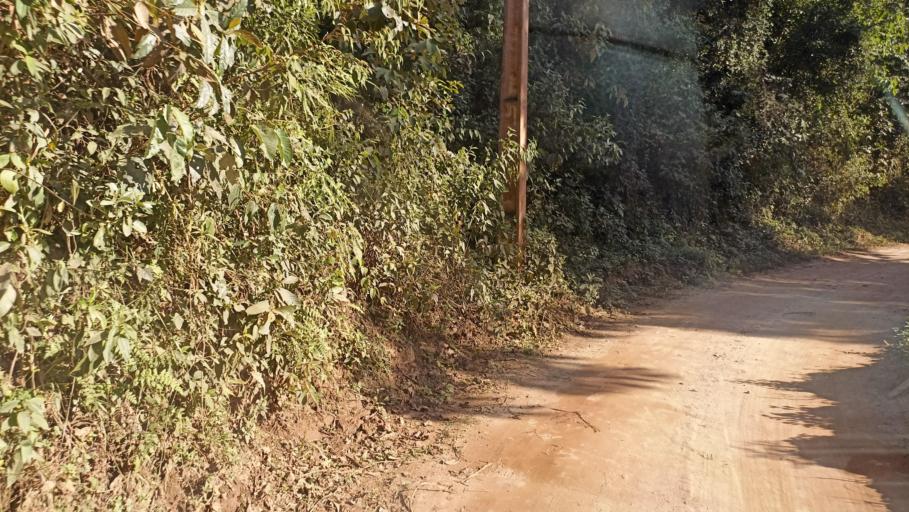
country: BR
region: Minas Gerais
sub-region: Ouro Preto
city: Ouro Preto
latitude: -20.3070
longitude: -43.5767
